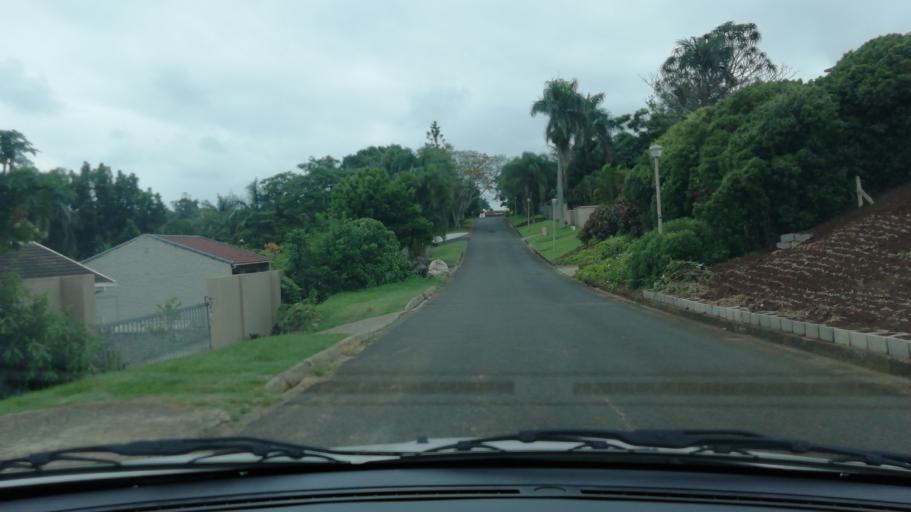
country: ZA
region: KwaZulu-Natal
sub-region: uThungulu District Municipality
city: Empangeni
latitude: -28.7562
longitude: 31.8860
